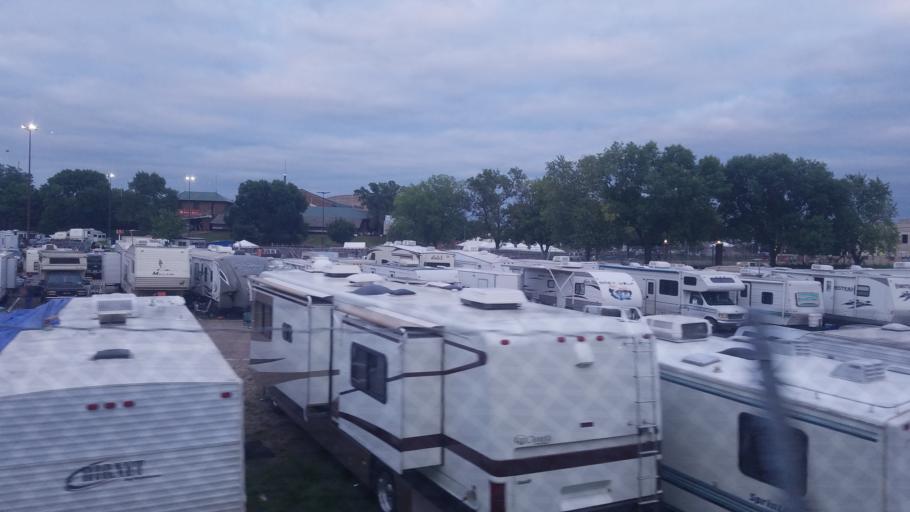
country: US
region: Minnesota
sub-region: Ramsey County
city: Falcon Heights
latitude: 44.9775
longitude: -93.1809
